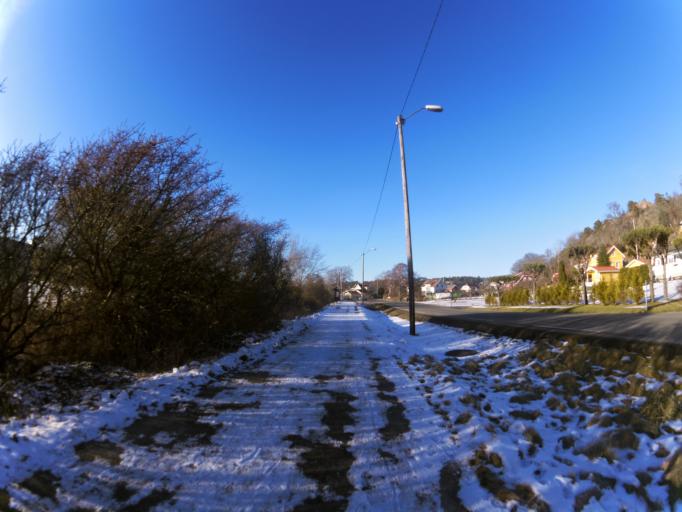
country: NO
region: Ostfold
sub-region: Fredrikstad
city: Lervik
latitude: 59.2141
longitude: 10.7927
